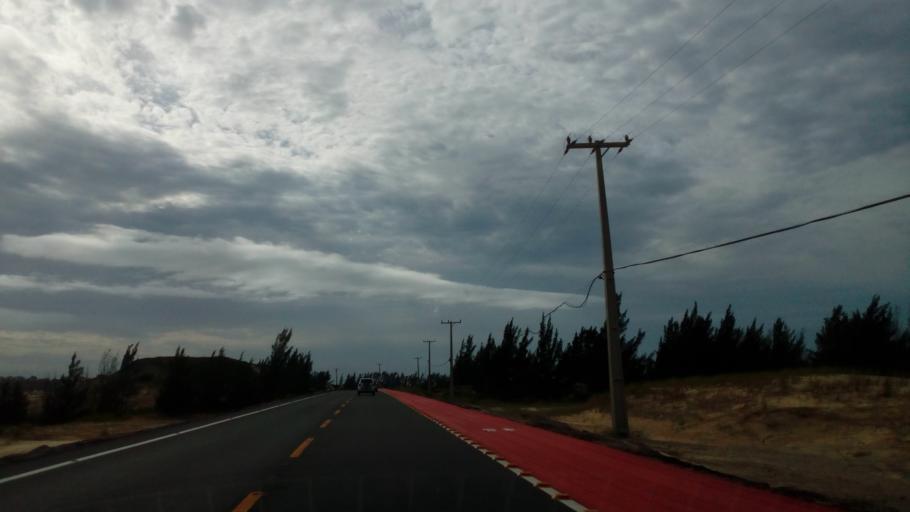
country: BR
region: Santa Catarina
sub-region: Laguna
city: Laguna
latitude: -28.6023
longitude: -48.8336
